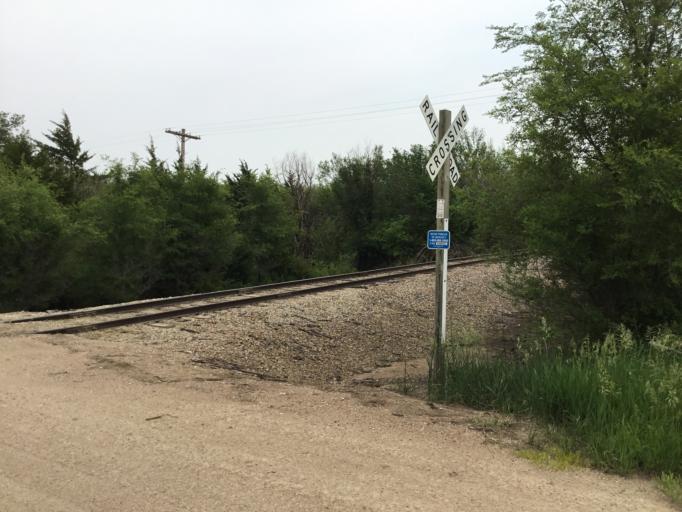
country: US
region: Kansas
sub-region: Republic County
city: Belleville
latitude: 39.7809
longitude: -97.8762
